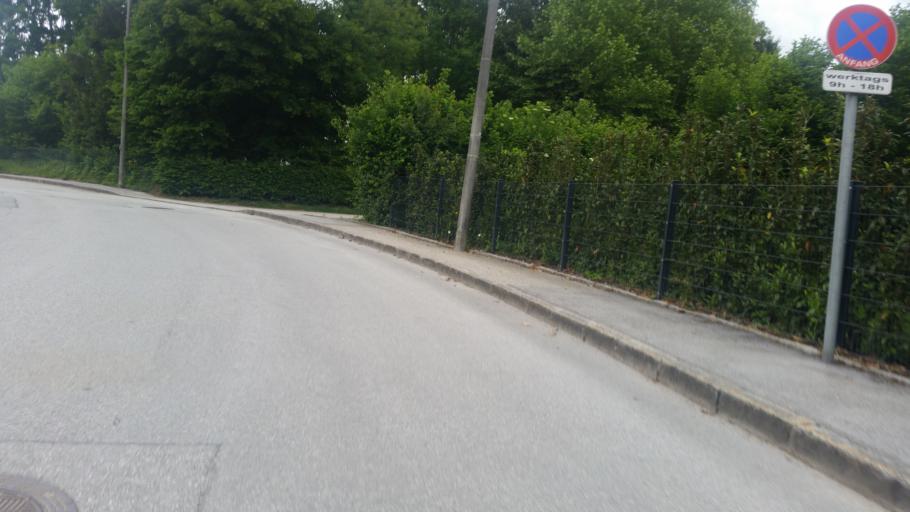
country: AT
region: Salzburg
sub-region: Salzburg Stadt
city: Salzburg
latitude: 47.7927
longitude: 13.0770
